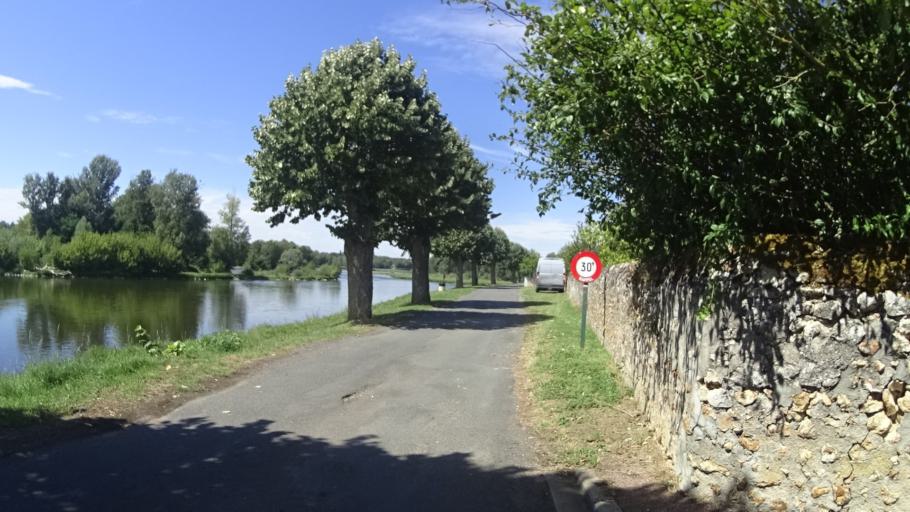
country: FR
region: Centre
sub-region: Departement du Loiret
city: Briare
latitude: 47.5886
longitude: 2.7842
